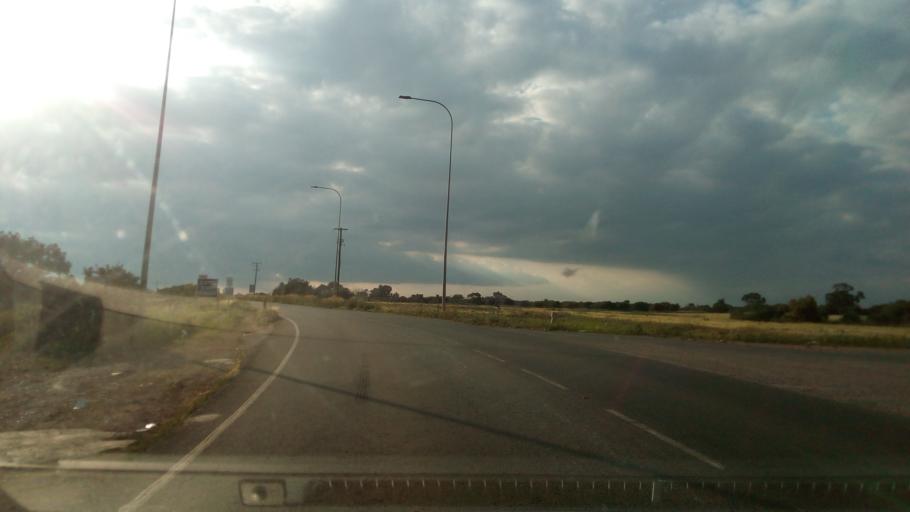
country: CY
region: Ammochostos
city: Liopetri
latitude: 34.9760
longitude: 33.8744
